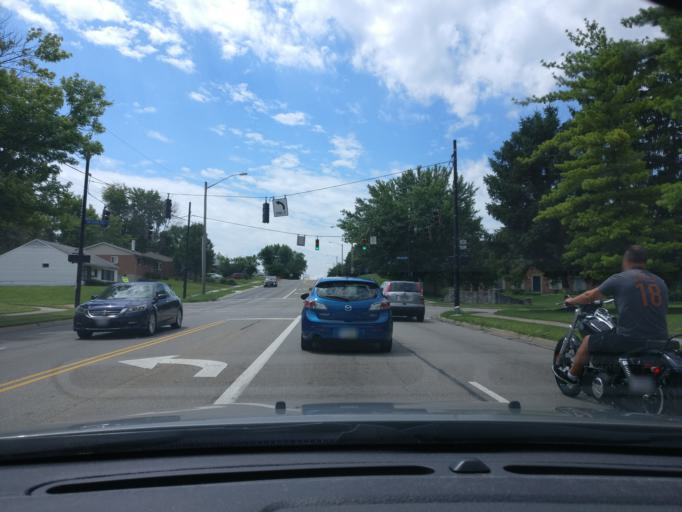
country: US
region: Ohio
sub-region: Montgomery County
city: West Carrollton City
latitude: 39.6590
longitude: -84.2421
